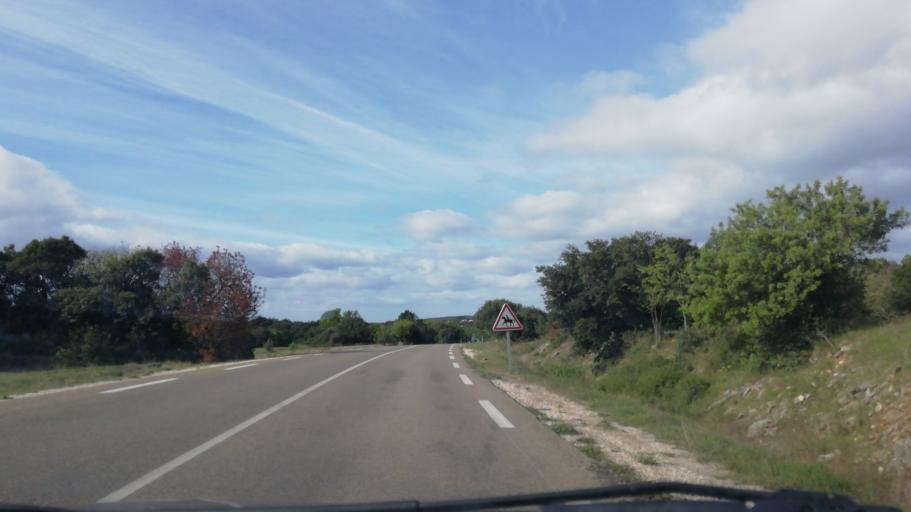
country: FR
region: Languedoc-Roussillon
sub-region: Departement de l'Herault
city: Saint-Martin-de-Londres
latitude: 43.7546
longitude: 3.7172
